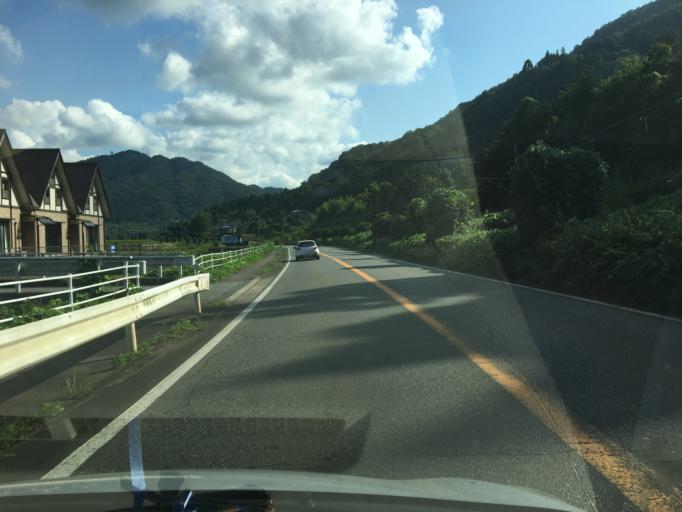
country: JP
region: Hyogo
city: Toyooka
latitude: 35.4303
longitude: 134.7876
